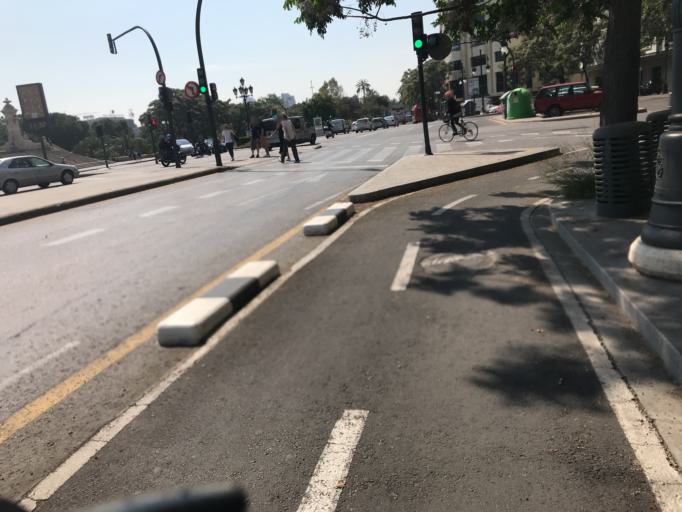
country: ES
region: Valencia
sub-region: Provincia de Valencia
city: Valencia
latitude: 39.4706
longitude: -0.3654
